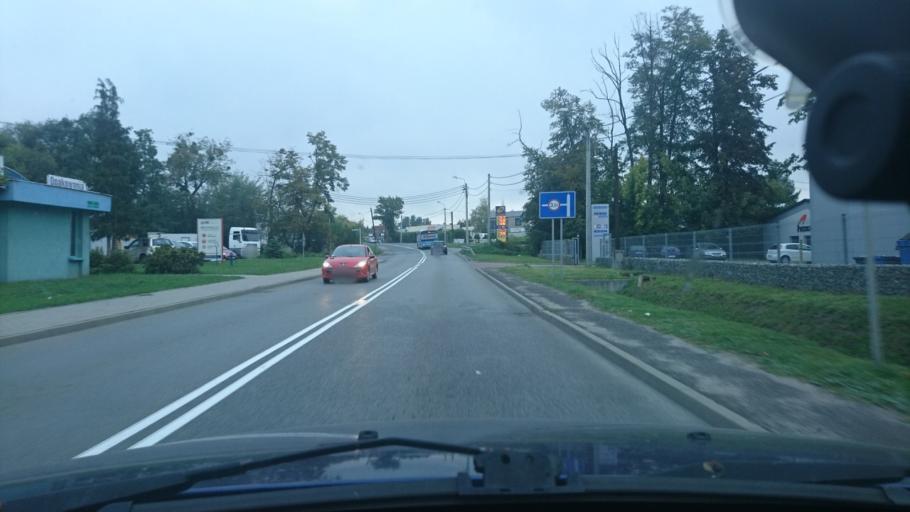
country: PL
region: Silesian Voivodeship
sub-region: Bielsko-Biala
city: Bielsko-Biala
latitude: 49.8579
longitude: 19.0351
